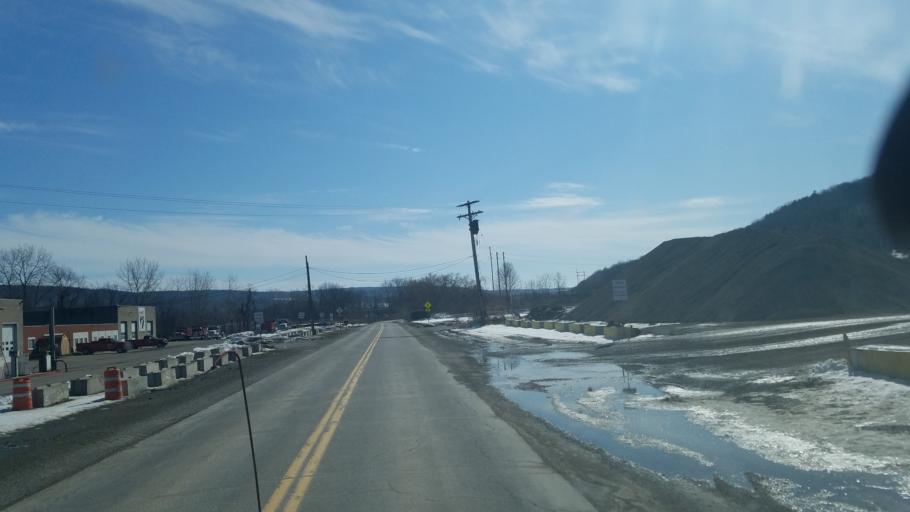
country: US
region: New York
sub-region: Steuben County
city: Hornell
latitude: 42.3704
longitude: -77.6870
